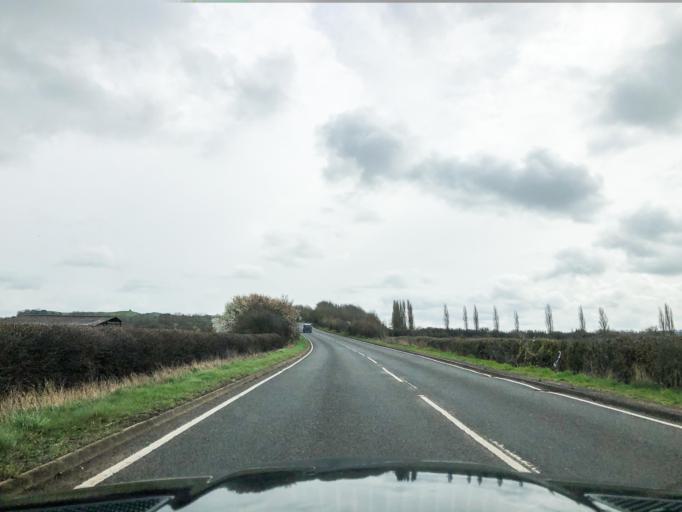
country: GB
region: England
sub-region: Warwickshire
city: Harbury
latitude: 52.1725
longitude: -1.4528
